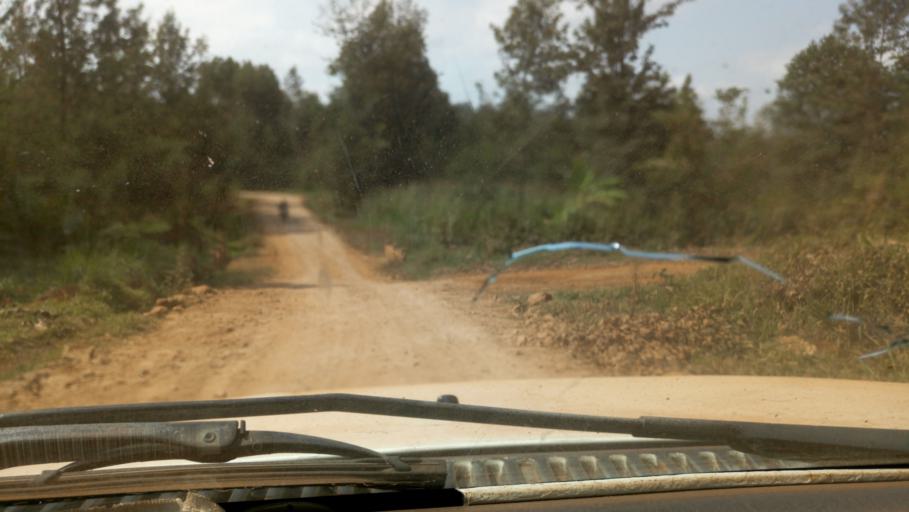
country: KE
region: Murang'a District
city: Kangema
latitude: -0.7528
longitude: 37.0148
